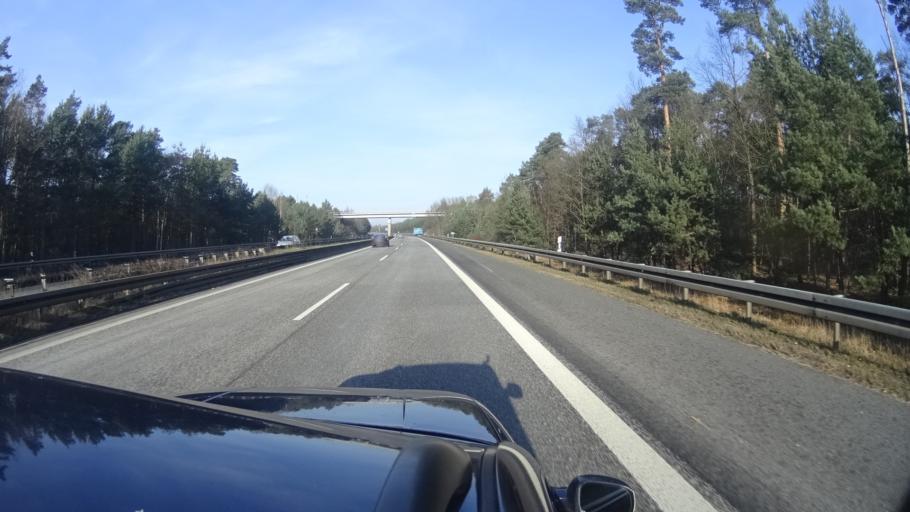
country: DE
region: Brandenburg
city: Hohen Neuendorf
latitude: 52.6647
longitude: 13.2413
